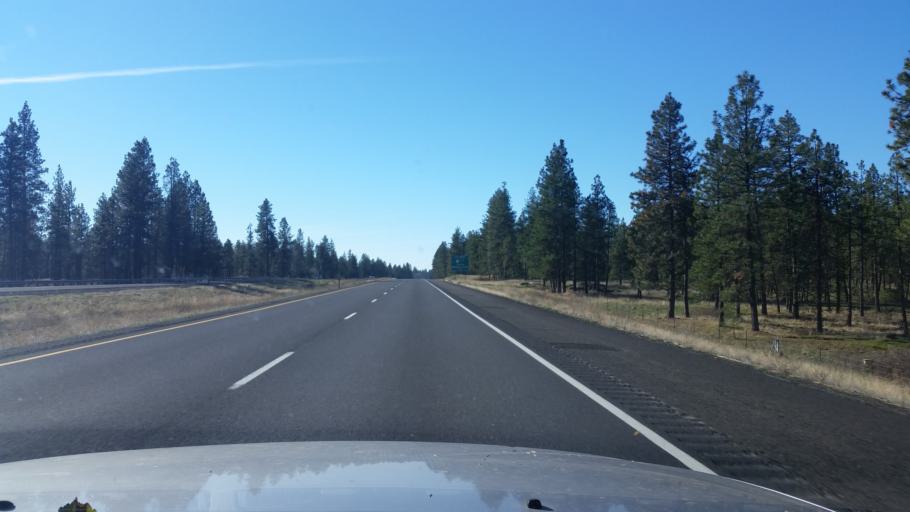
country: US
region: Washington
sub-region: Spokane County
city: Medical Lake
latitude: 47.5190
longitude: -117.6706
